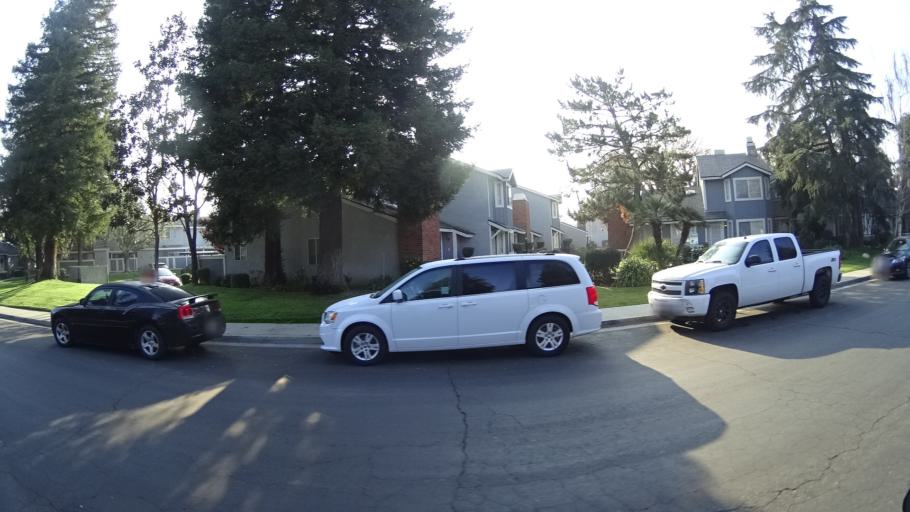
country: US
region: California
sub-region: Kern County
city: Greenacres
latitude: 35.3327
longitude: -119.0941
